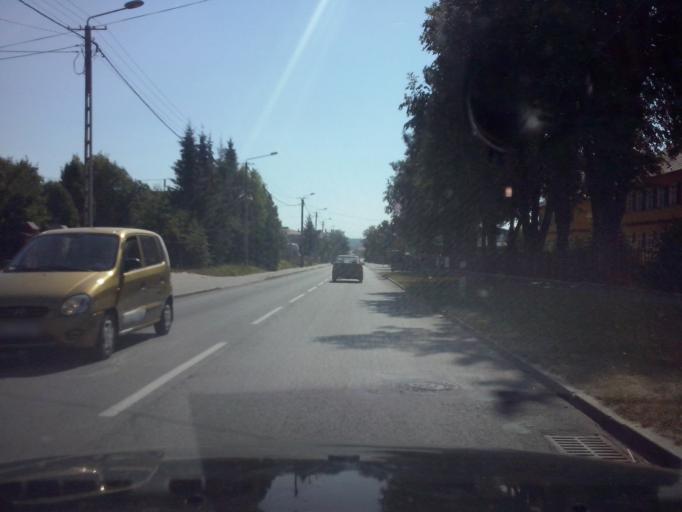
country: PL
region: Swietokrzyskie
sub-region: Powiat kielecki
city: Daleszyce
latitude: 50.8039
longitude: 20.8023
